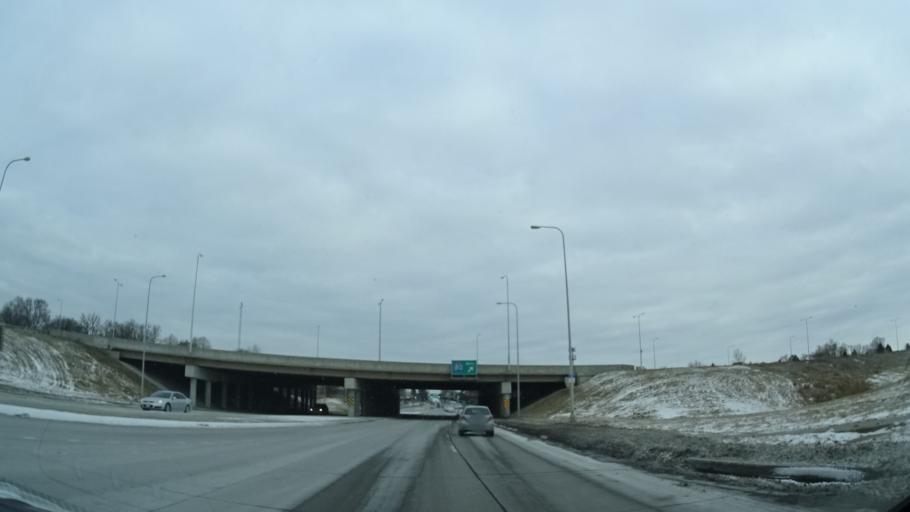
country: US
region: Nebraska
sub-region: Douglas County
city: Omaha
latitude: 41.2236
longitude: -95.9757
